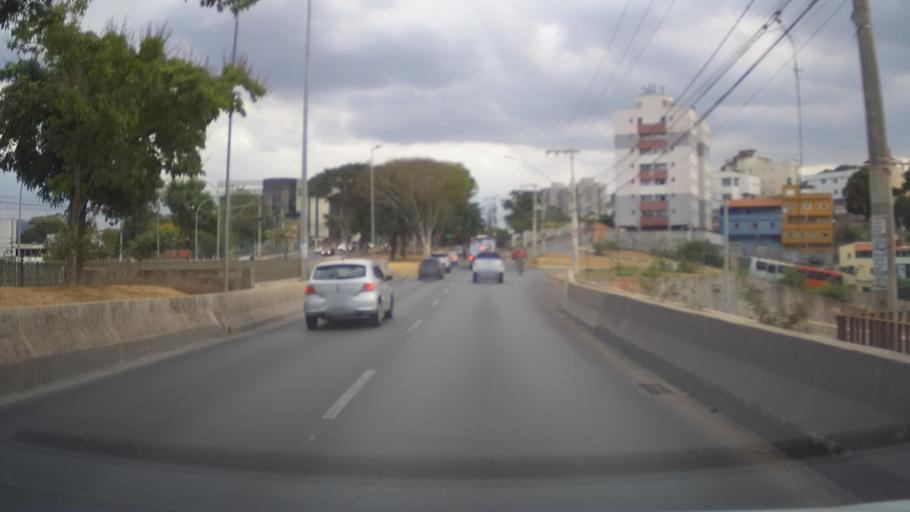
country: BR
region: Minas Gerais
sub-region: Belo Horizonte
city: Belo Horizonte
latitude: -19.8817
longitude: -43.9145
